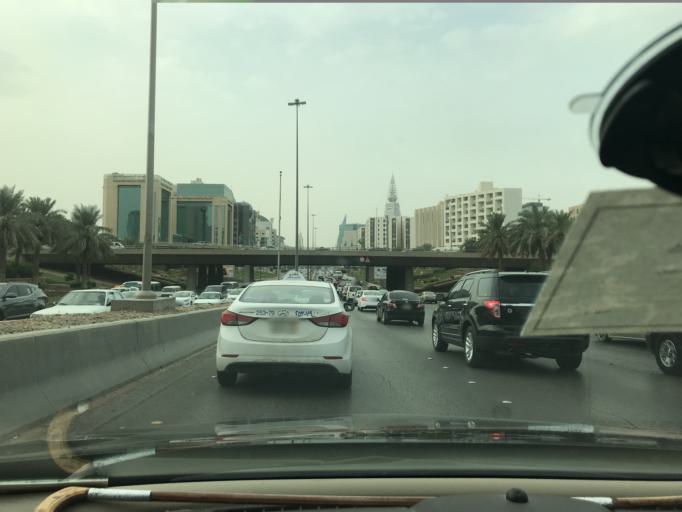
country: SA
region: Ar Riyad
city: Riyadh
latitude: 24.6777
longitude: 46.6894
